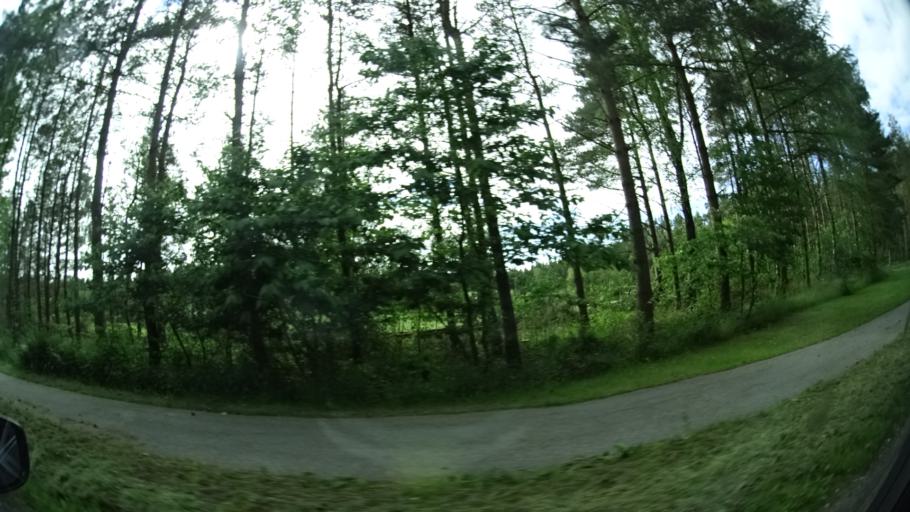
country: DK
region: Central Jutland
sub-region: Norddjurs Kommune
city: Grenaa
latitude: 56.4850
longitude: 10.7317
